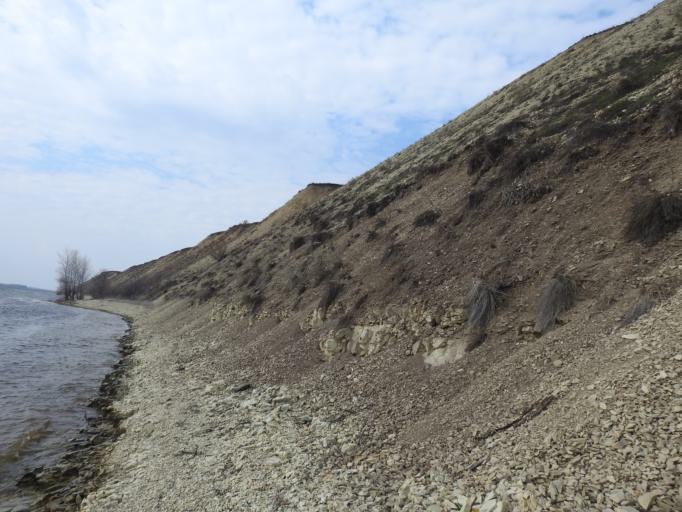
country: RU
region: Saratov
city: Voskresenskoye
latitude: 51.8048
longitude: 46.9121
